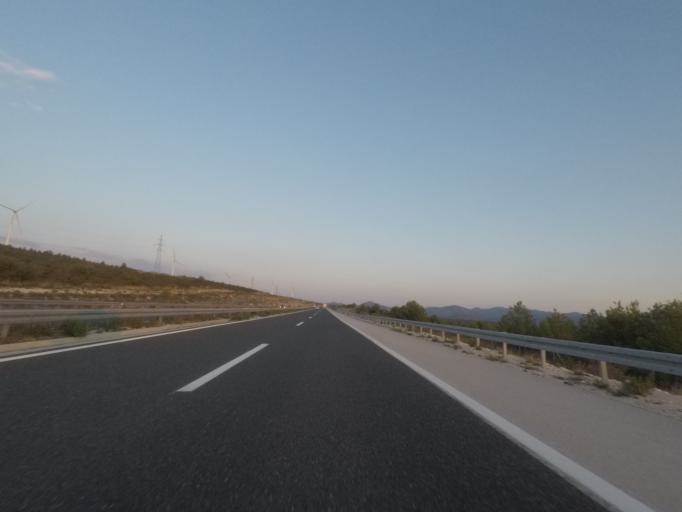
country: HR
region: Sibensko-Kniniska
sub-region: Grad Sibenik
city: Brodarica
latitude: 43.7078
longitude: 15.9958
